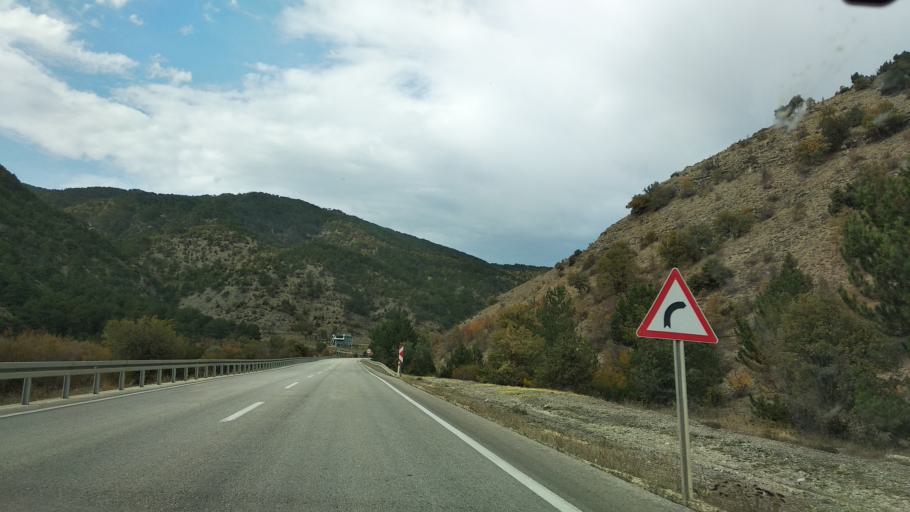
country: TR
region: Bolu
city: Mudurnu
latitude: 40.3387
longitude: 31.2445
